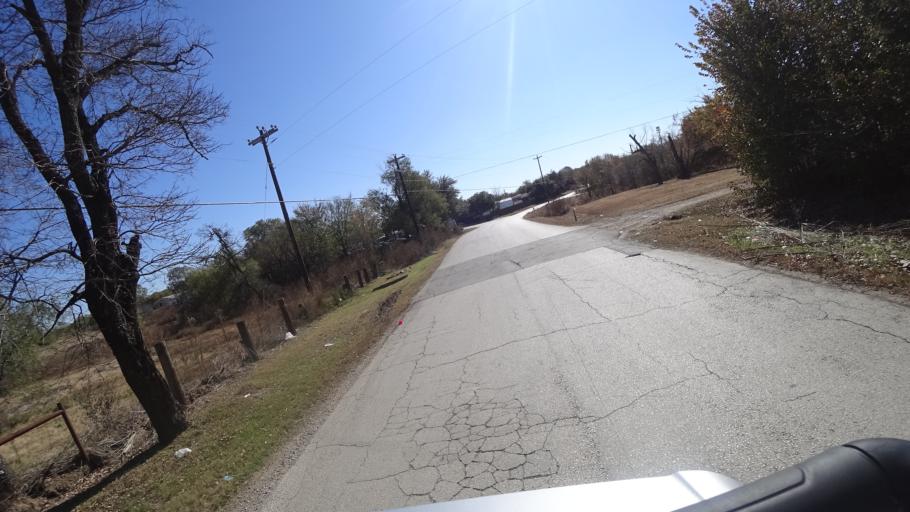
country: US
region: Texas
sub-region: Denton County
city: Lewisville
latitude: 33.0417
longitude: -96.9363
